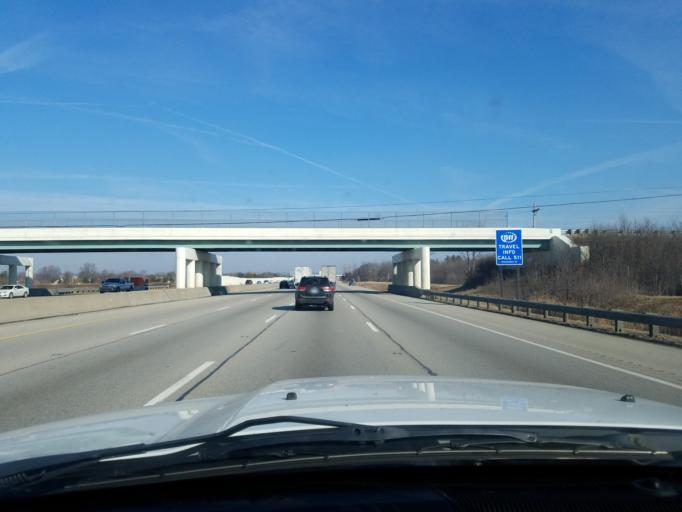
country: US
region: Ohio
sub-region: Butler County
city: Wetherington
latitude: 39.3831
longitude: -84.3642
